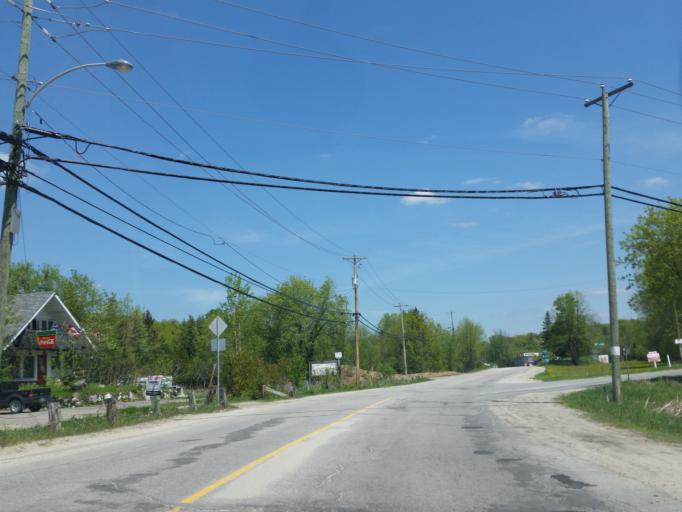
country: CA
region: Quebec
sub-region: Outaouais
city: Wakefield
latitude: 45.6470
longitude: -75.9278
